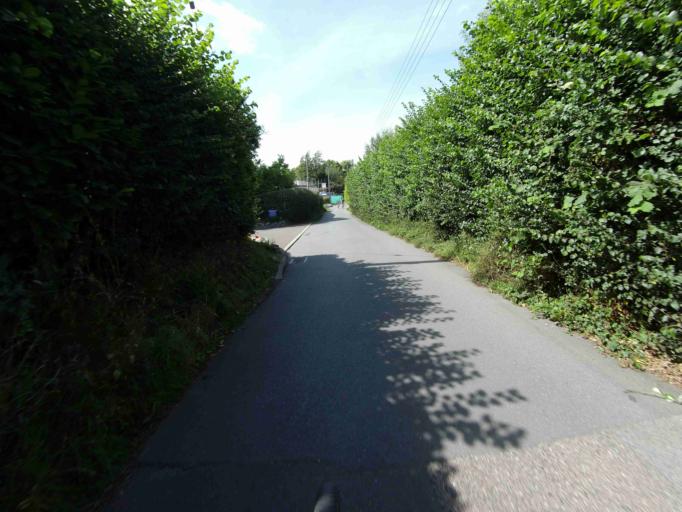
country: GB
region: England
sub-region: Devon
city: Topsham
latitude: 50.6716
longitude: -3.4434
